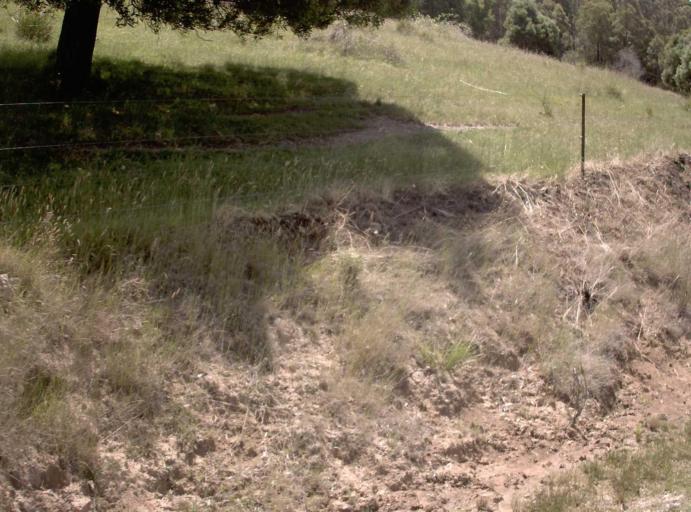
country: AU
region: New South Wales
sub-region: Bombala
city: Bombala
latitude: -37.3784
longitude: 149.0128
